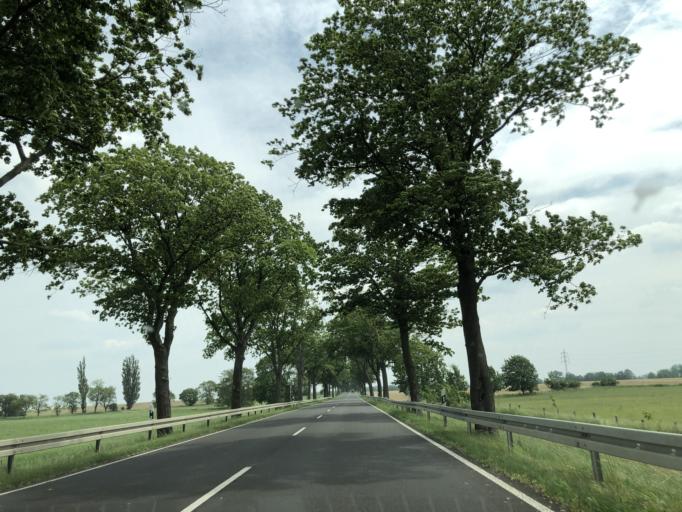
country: DE
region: Brandenburg
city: Kyritz
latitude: 52.9601
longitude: 12.3458
